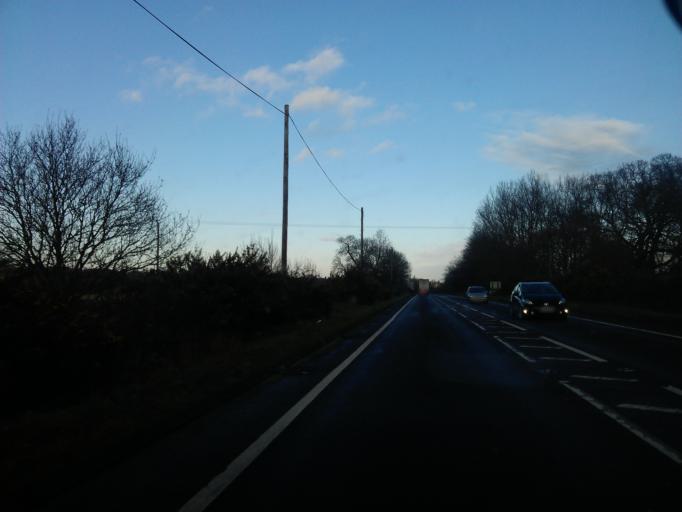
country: GB
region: England
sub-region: Suffolk
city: Shotley Gate
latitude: 51.9308
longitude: 1.2226
